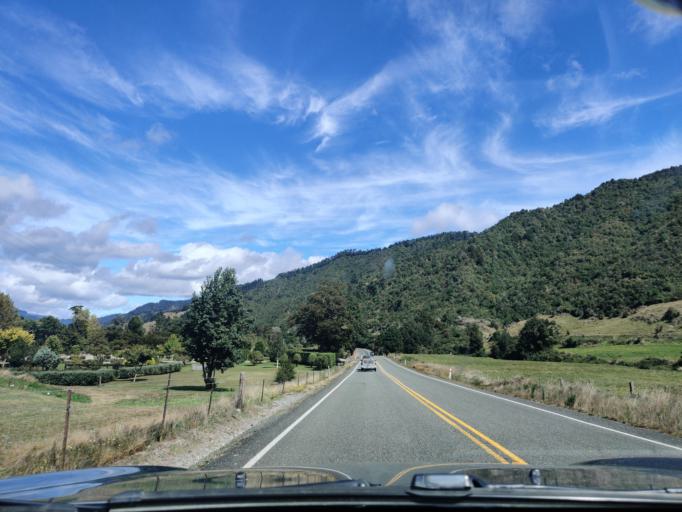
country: NZ
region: Tasman
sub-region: Tasman District
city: Wakefield
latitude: -41.7102
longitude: 172.4173
